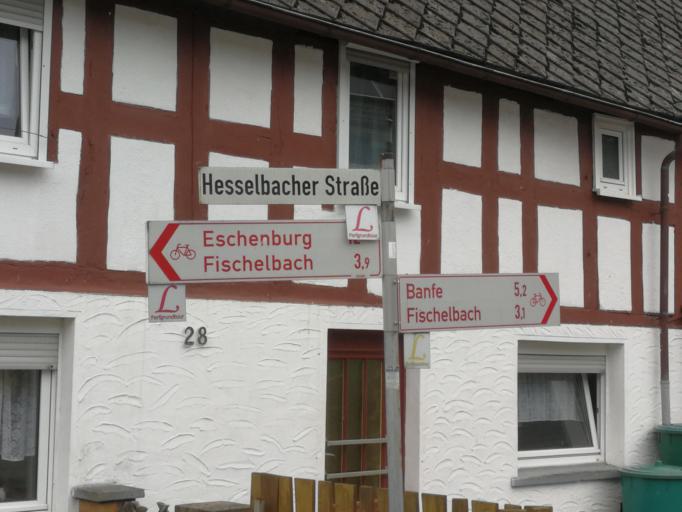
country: DE
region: North Rhine-Westphalia
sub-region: Regierungsbezirk Arnsberg
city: Bad Laasphe
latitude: 50.8854
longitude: 8.3679
